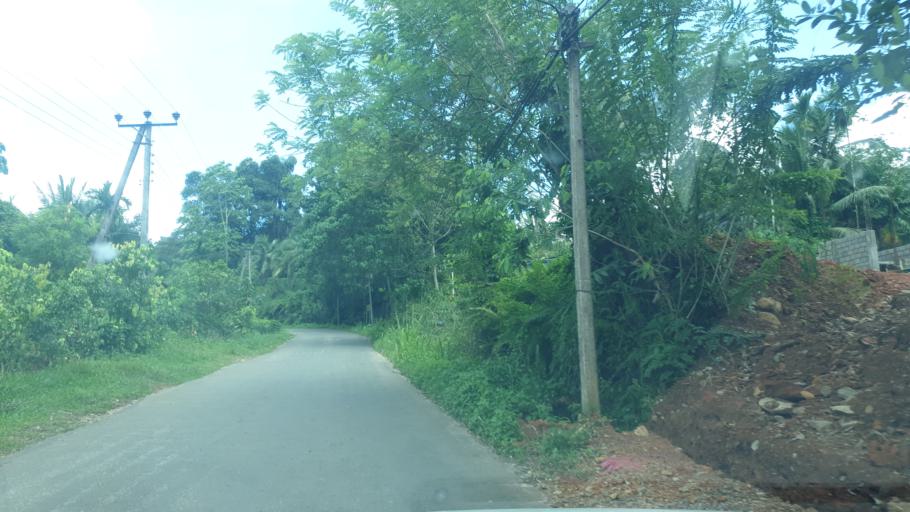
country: LK
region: Sabaragamuwa
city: Ratnapura
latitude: 6.4909
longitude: 80.3989
